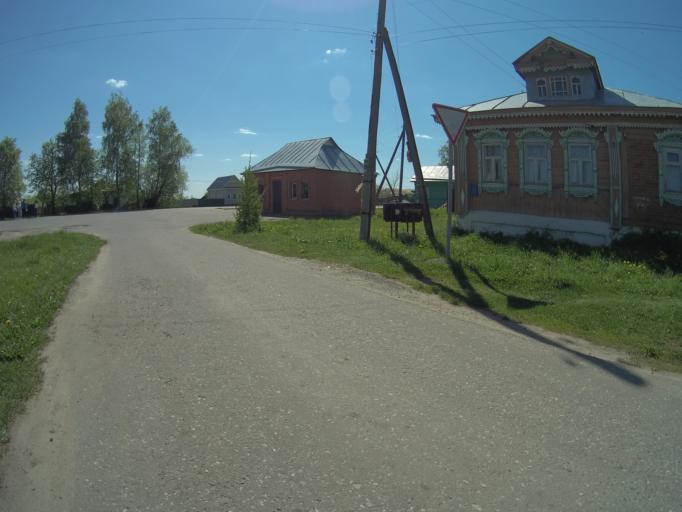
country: RU
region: Vladimir
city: Kideksha
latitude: 56.4241
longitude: 40.5264
